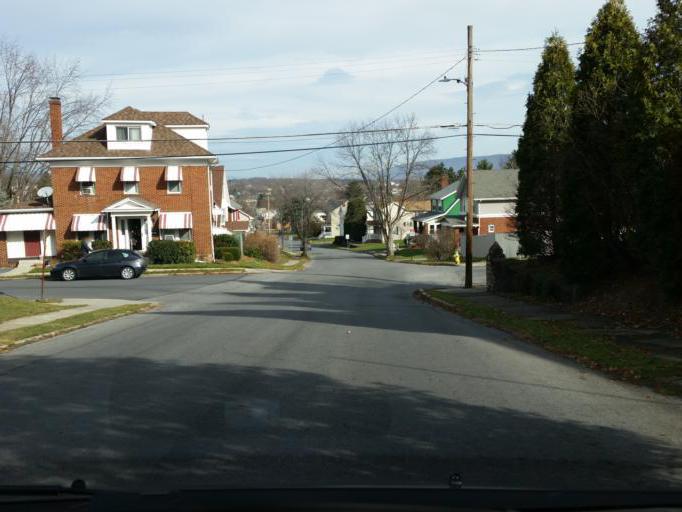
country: US
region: Pennsylvania
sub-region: Blair County
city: Altoona
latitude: 40.5255
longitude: -78.4103
